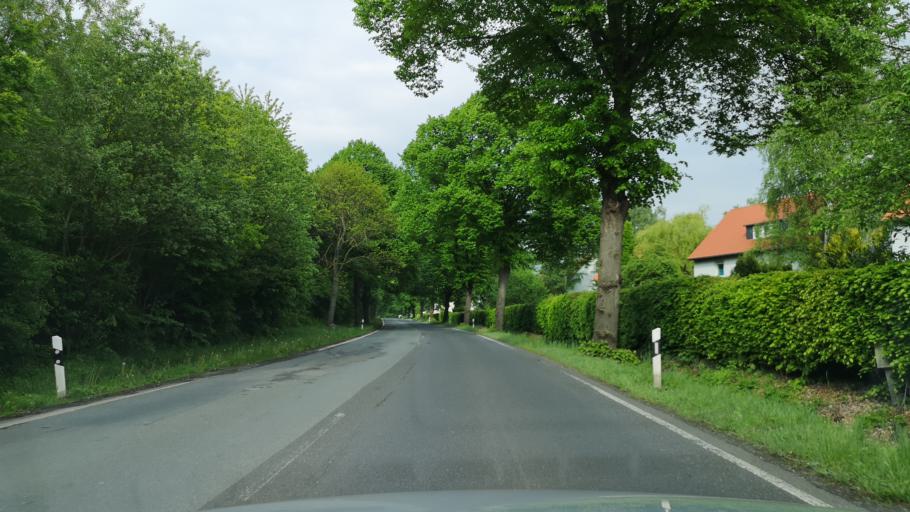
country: DE
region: North Rhine-Westphalia
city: Iserlohn
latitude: 51.4161
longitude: 7.7015
